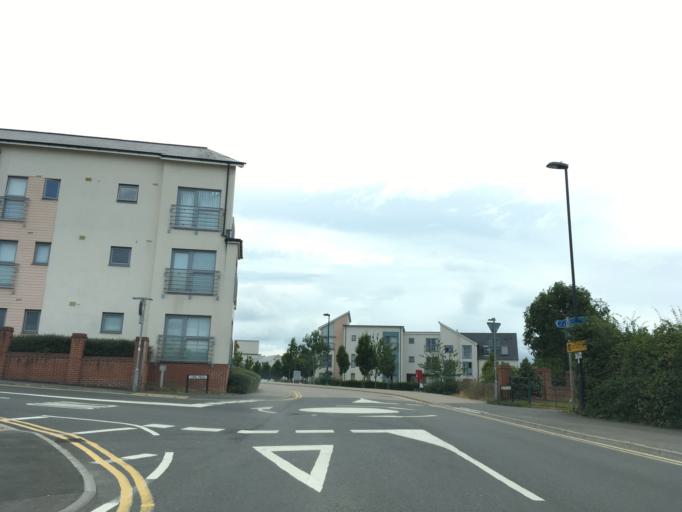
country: GB
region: England
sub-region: South Gloucestershire
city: Stoke Gifford
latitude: 51.5005
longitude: -2.5595
